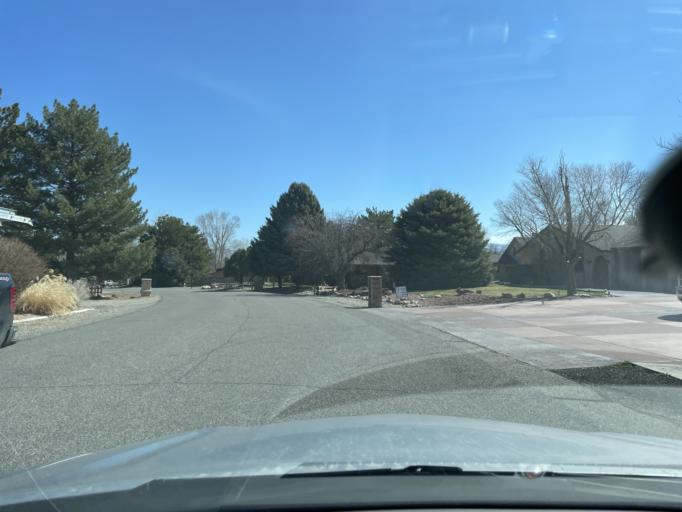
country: US
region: Colorado
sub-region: Mesa County
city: Redlands
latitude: 39.0805
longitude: -108.6735
